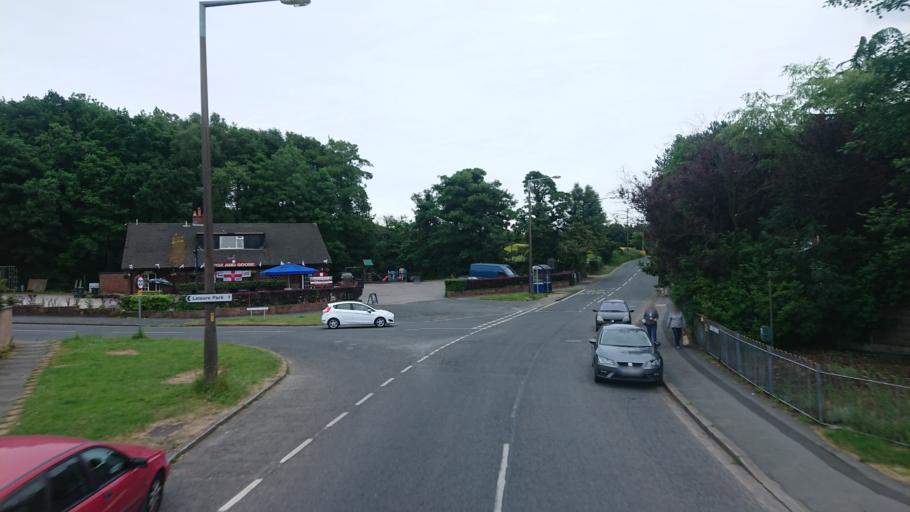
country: GB
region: England
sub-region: Lancashire
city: Lancaster
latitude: 54.0315
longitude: -2.7824
